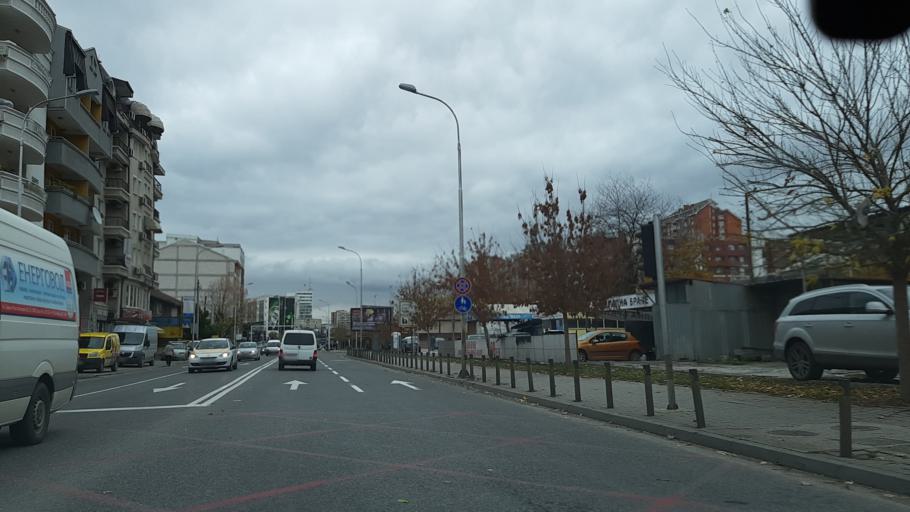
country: MK
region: Karpos
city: Skopje
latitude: 41.9949
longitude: 21.4152
